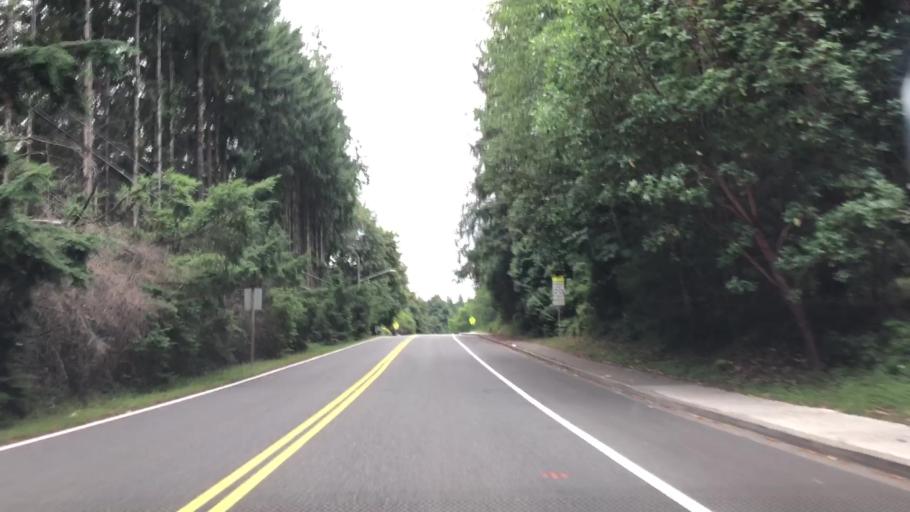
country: US
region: Washington
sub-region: King County
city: Woodinville
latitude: 47.7843
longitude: -122.1567
